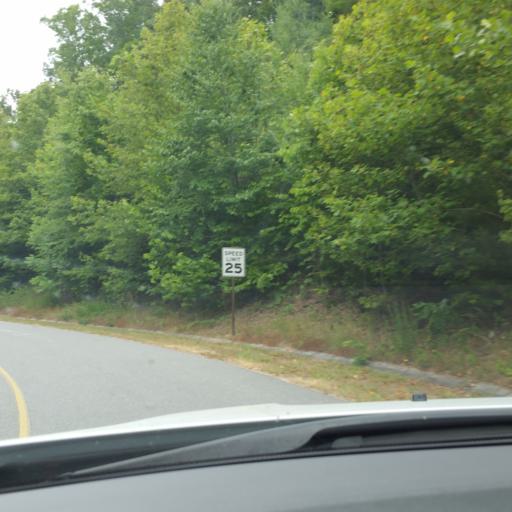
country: US
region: North Carolina
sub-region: Buncombe County
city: Biltmore Forest
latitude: 35.5680
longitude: -82.4850
